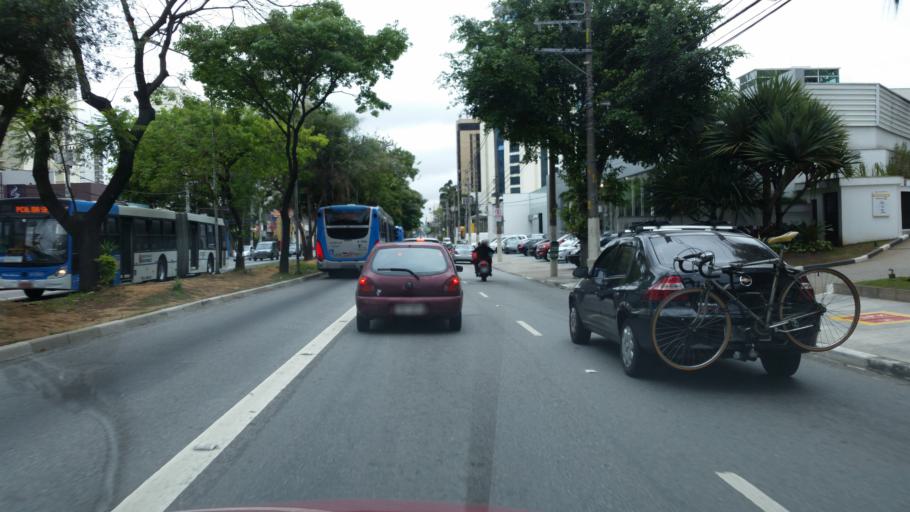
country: BR
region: Sao Paulo
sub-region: Sao Paulo
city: Sao Paulo
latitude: -23.6043
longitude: -46.6630
